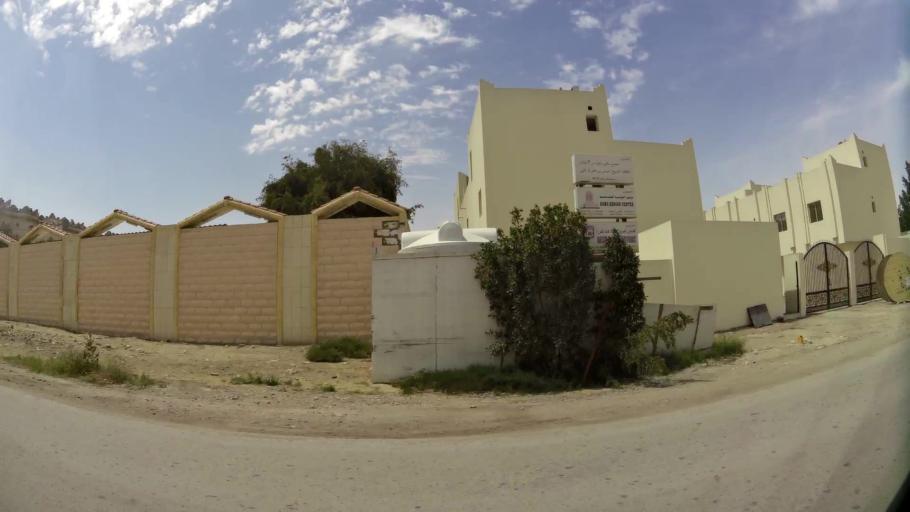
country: QA
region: Baladiyat ar Rayyan
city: Ar Rayyan
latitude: 25.2749
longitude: 51.4261
